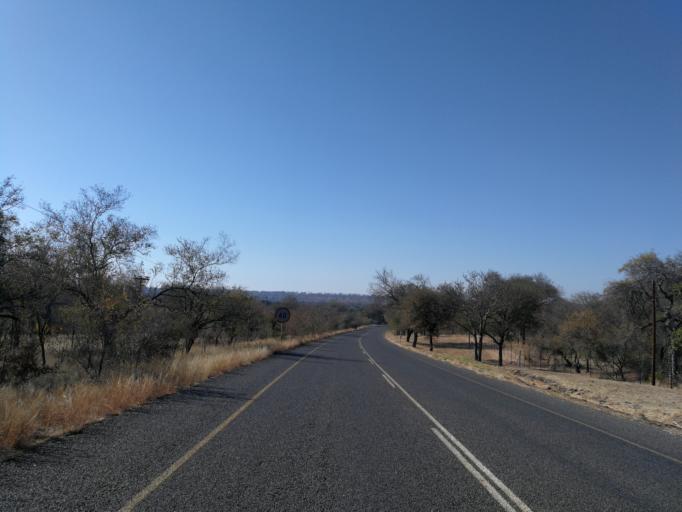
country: ZA
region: Limpopo
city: Thulamahashi
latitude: -24.9764
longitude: 31.4763
